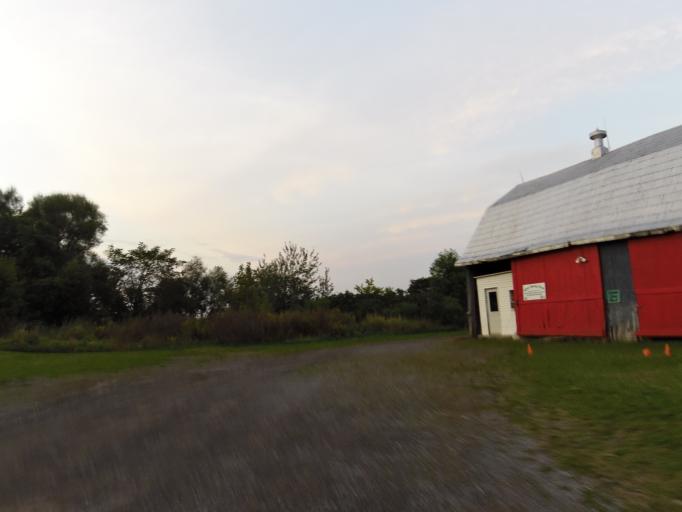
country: CA
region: Ontario
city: Bells Corners
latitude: 45.3344
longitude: -75.8153
